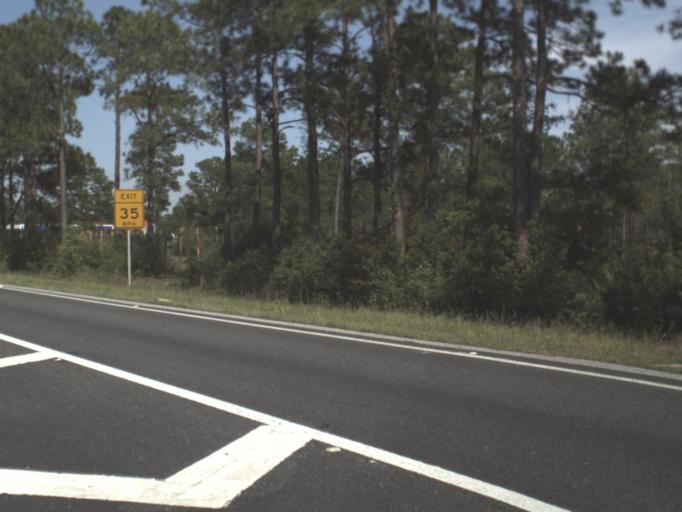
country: US
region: Florida
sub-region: Santa Rosa County
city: Bagdad
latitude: 30.5670
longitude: -87.0350
